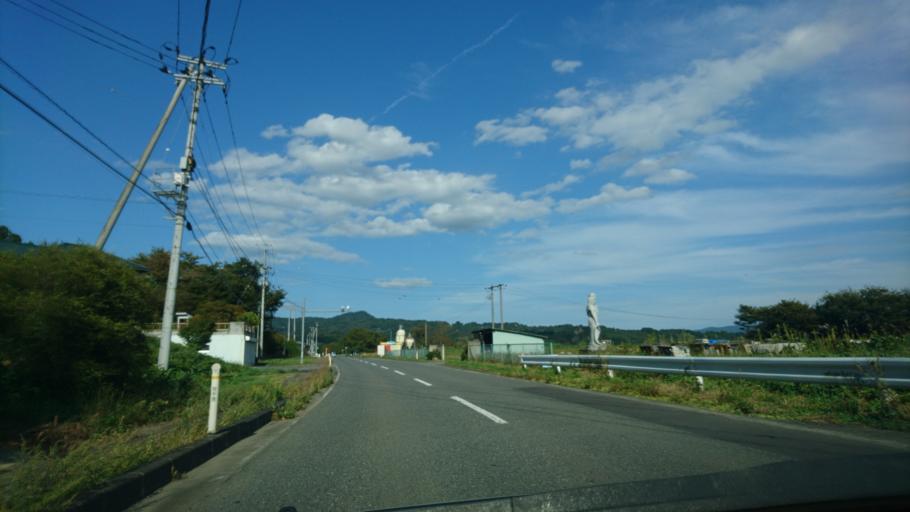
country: JP
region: Iwate
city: Ichinoseki
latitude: 38.8493
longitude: 141.2748
